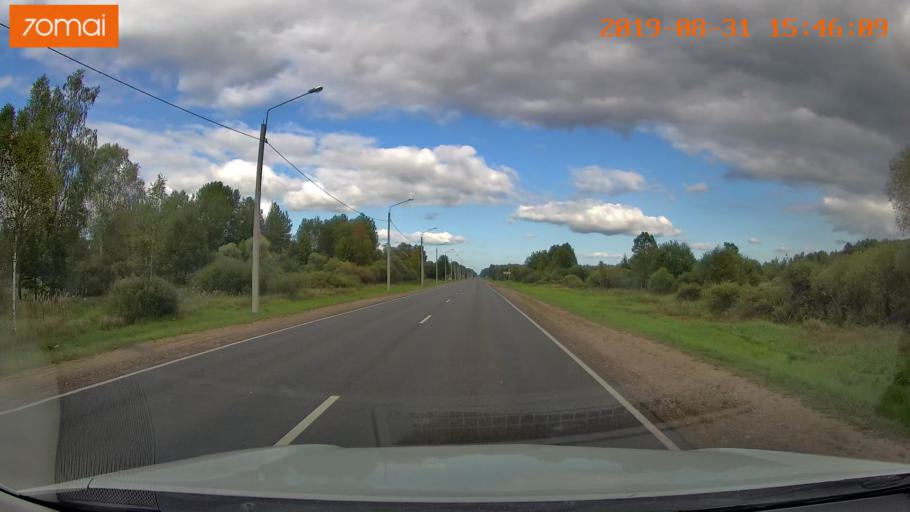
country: RU
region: Kaluga
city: Mosal'sk
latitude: 54.6710
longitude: 34.9767
